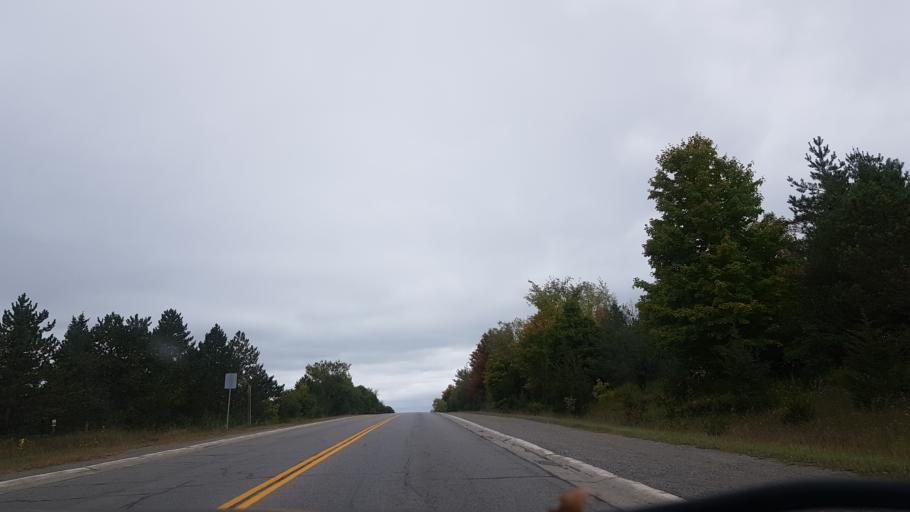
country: CA
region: Ontario
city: Peterborough
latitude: 44.2628
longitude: -78.3707
